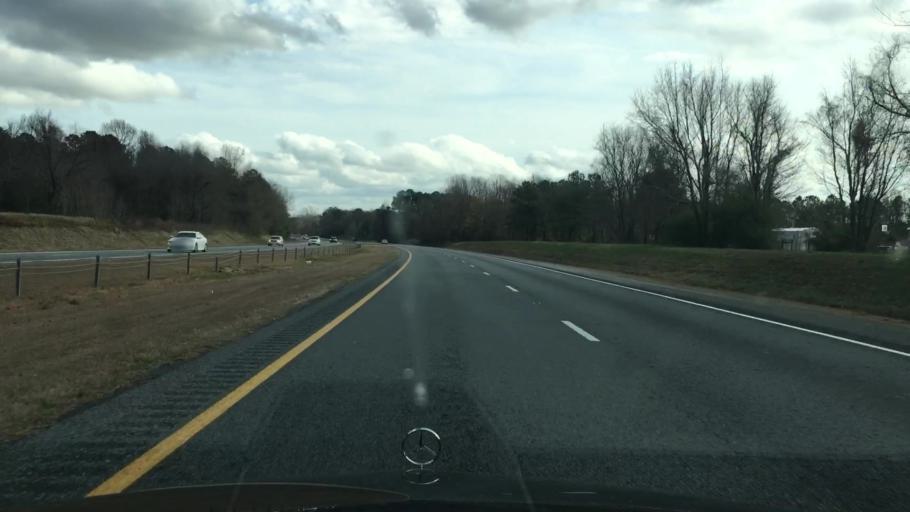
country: US
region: North Carolina
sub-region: Sampson County
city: Clinton
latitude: 35.2134
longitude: -78.3275
